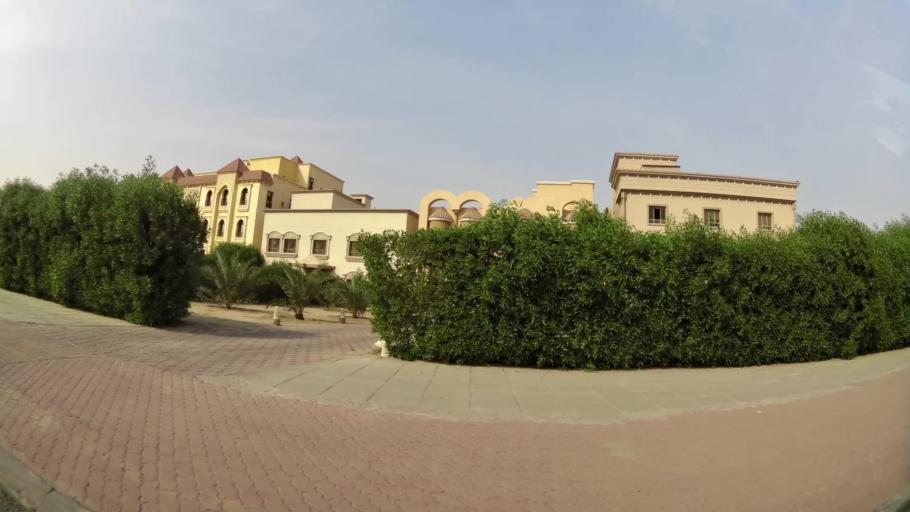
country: KW
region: Al Asimah
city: Ar Rabiyah
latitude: 29.2750
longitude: 47.9282
